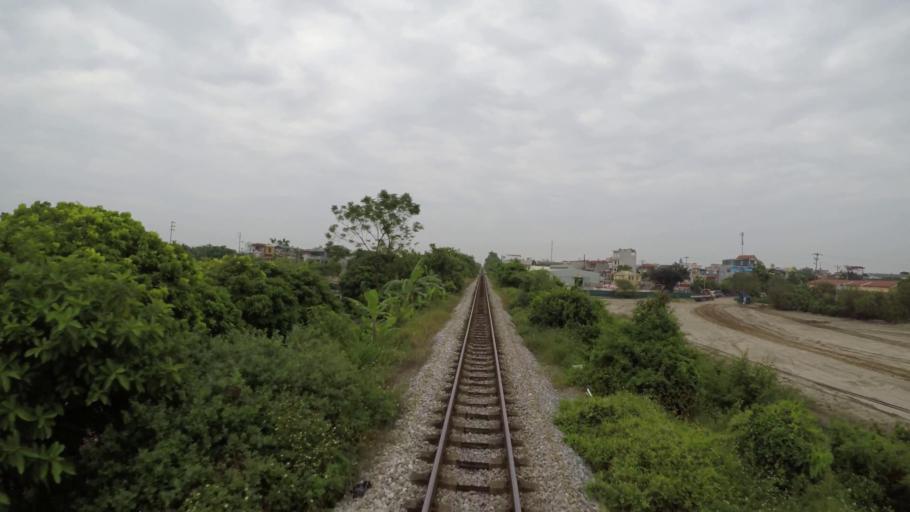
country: VN
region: Hai Duong
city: Thanh Pho Hai Duong
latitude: 20.9485
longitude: 106.3617
